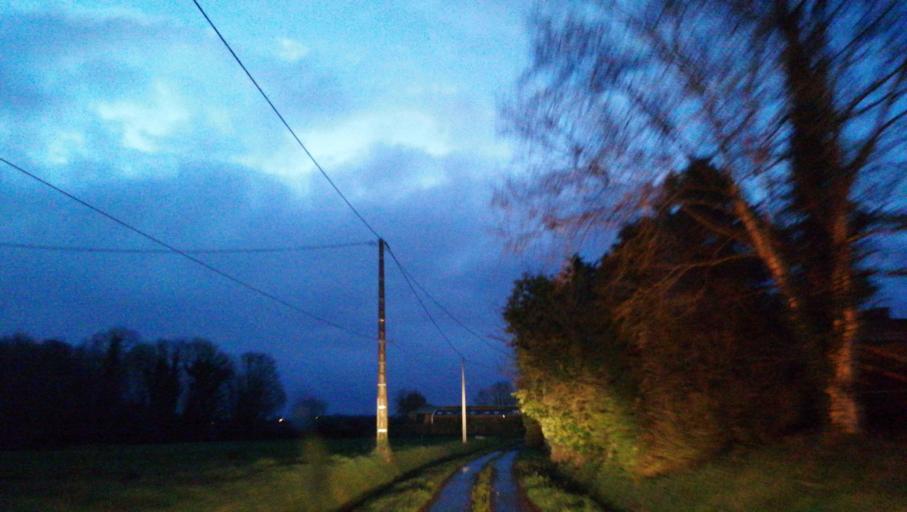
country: FR
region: Brittany
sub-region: Departement des Cotes-d'Armor
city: Plelo
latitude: 48.5633
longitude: -2.9680
